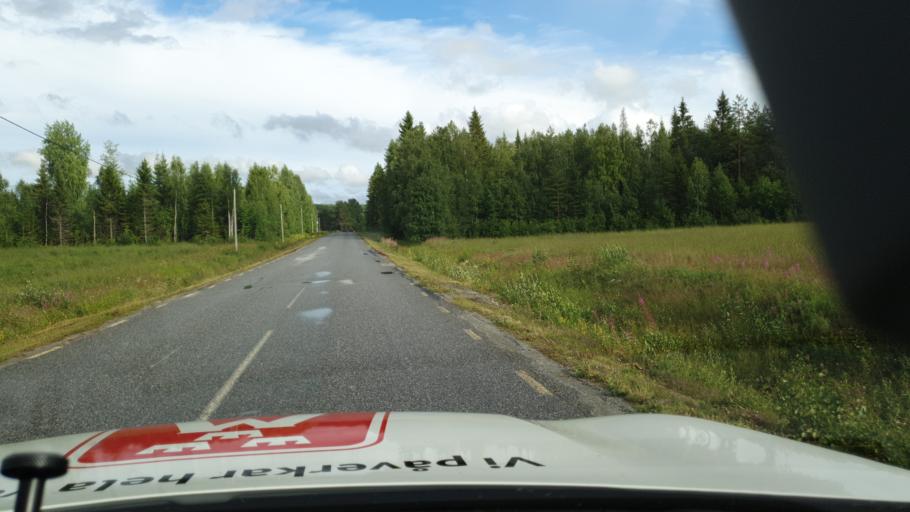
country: SE
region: Vaesterbotten
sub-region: Skelleftea Kommun
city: Viken
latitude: 64.5193
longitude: 20.9753
